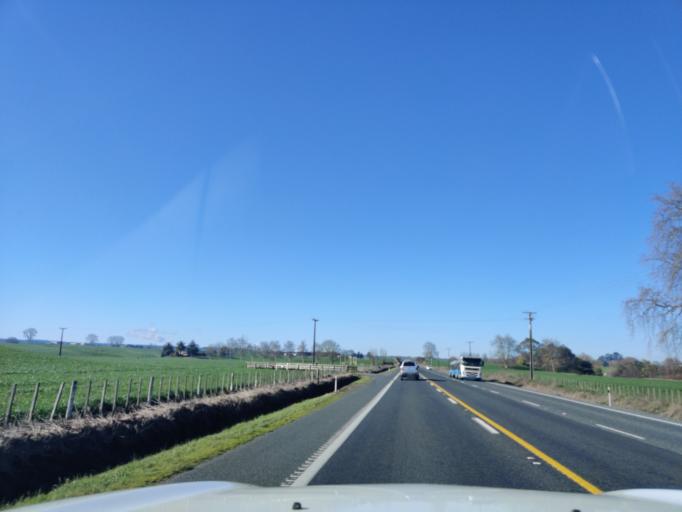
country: NZ
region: Waikato
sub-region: Matamata-Piako District
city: Matamata
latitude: -38.0195
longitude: 175.7820
